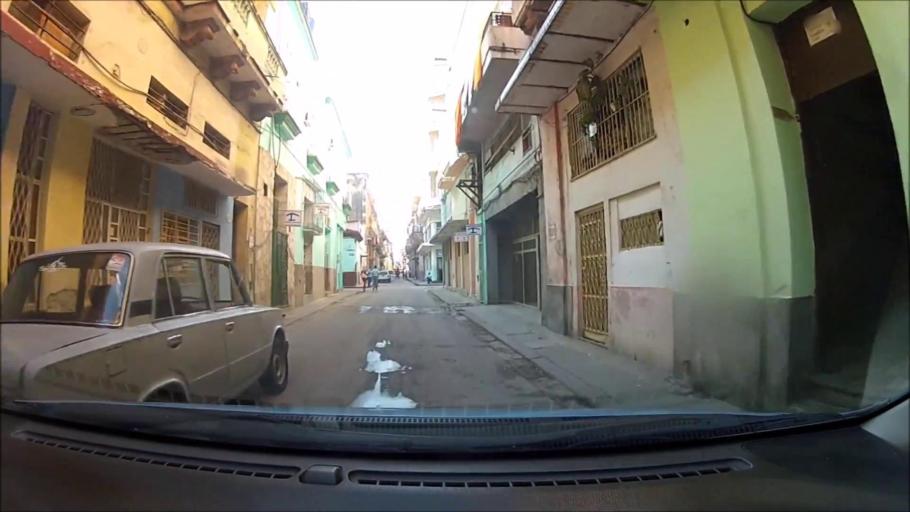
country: CU
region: La Habana
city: Centro Habana
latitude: 23.1363
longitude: -82.3643
